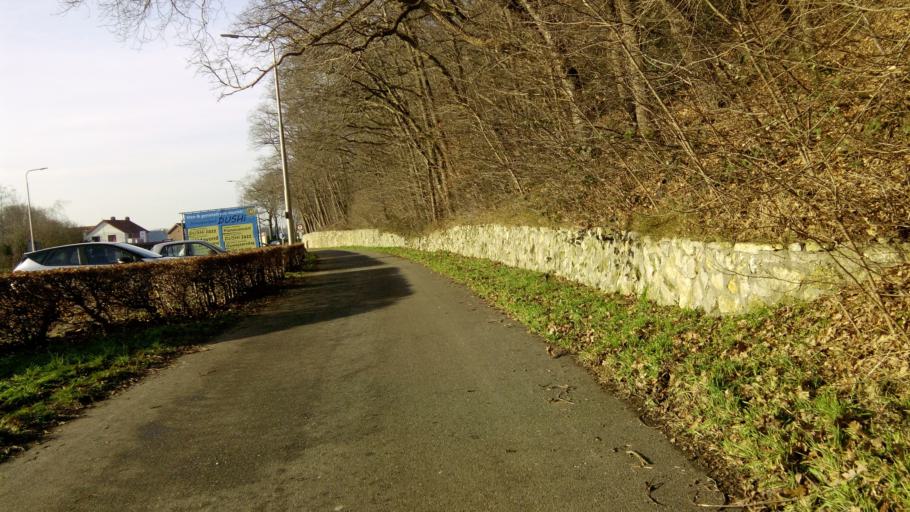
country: NL
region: Gelderland
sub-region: Gemeente Groesbeek
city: Bredeweg
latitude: 51.7383
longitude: 5.9199
